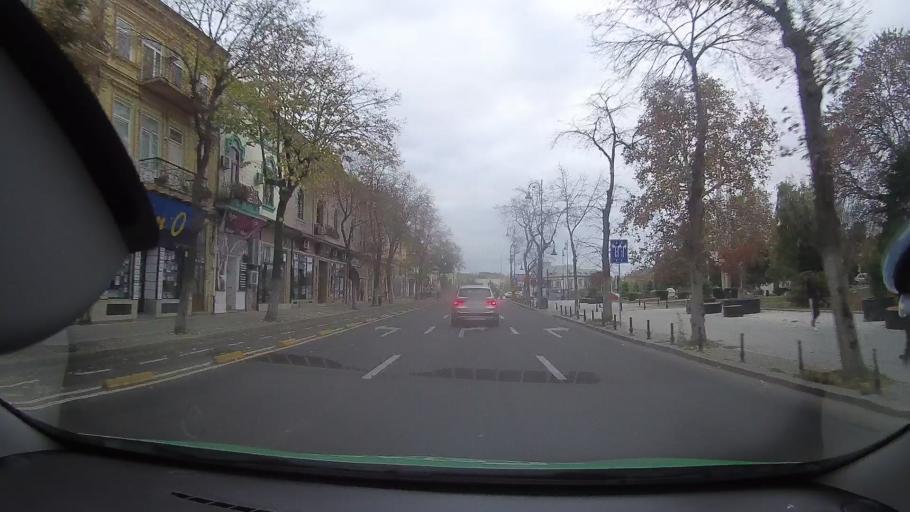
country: RO
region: Constanta
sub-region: Municipiul Constanta
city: Constanta
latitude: 44.1773
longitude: 28.6529
